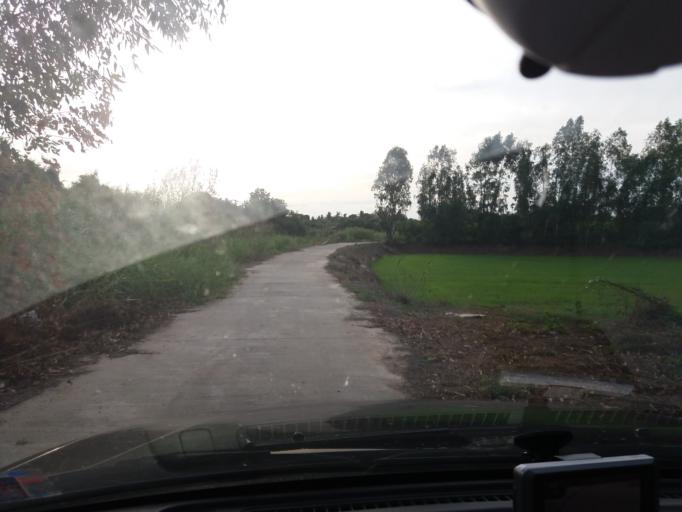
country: TH
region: Suphan Buri
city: Doembang Nangbuat
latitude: 14.8121
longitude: 100.1412
